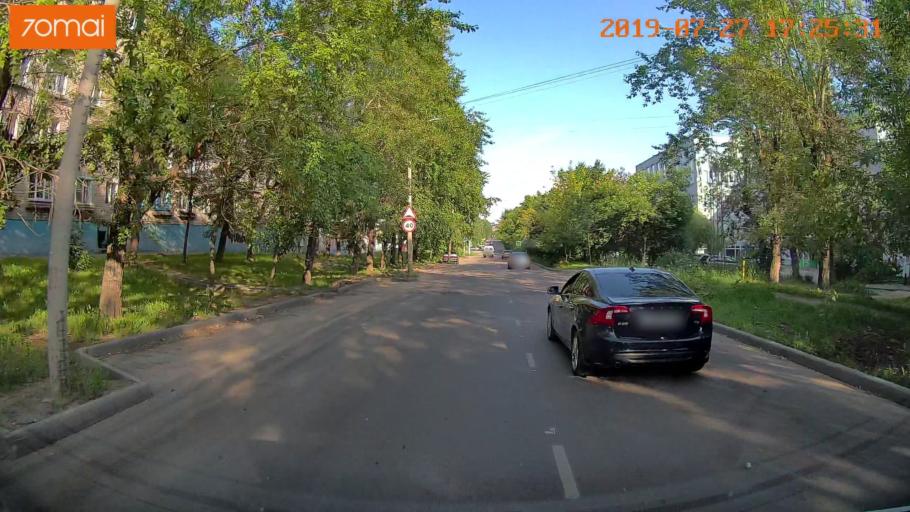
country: RU
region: Ivanovo
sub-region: Gorod Ivanovo
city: Ivanovo
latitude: 57.0171
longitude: 40.9597
